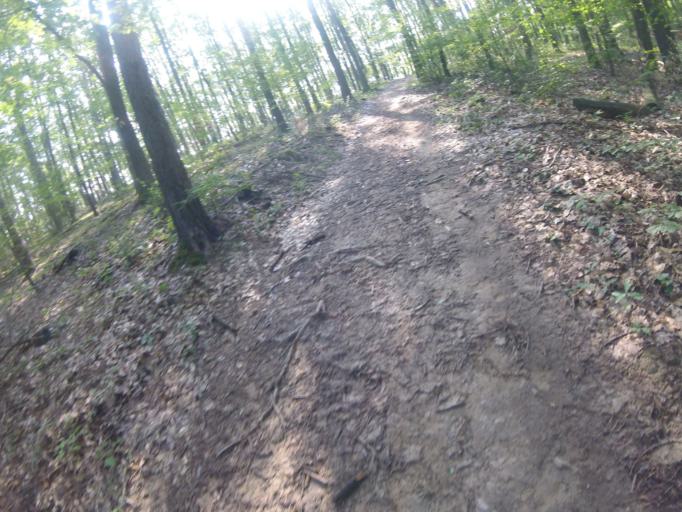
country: HU
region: Borsod-Abauj-Zemplen
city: Satoraljaujhely
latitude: 48.4481
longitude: 21.5742
